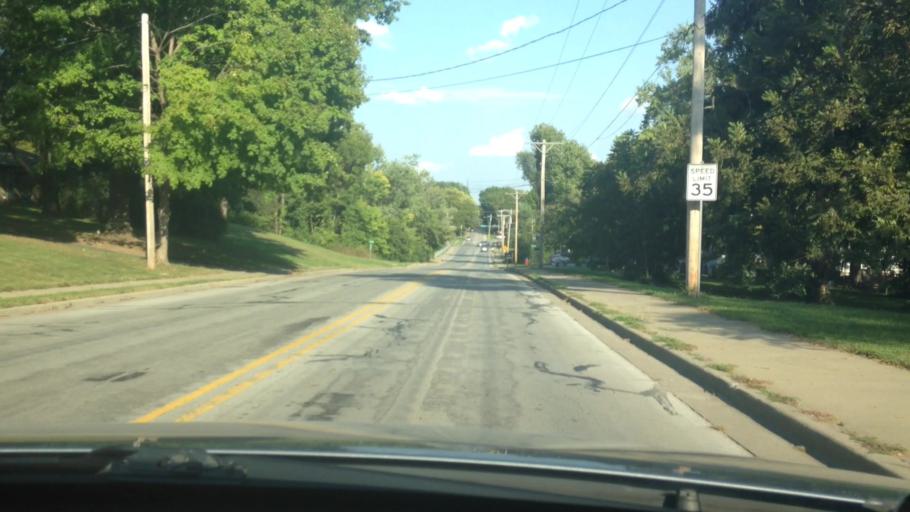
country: US
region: Kansas
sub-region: Leavenworth County
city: Leavenworth
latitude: 39.3177
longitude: -94.9319
